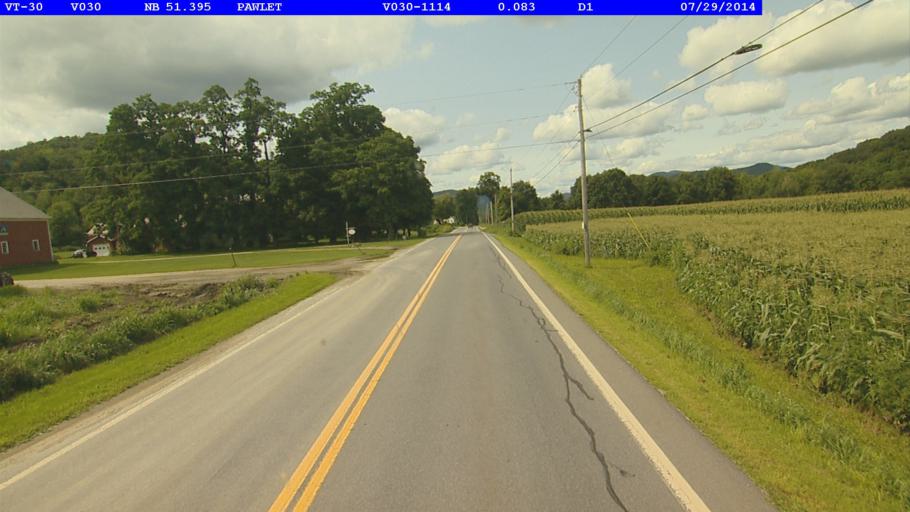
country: US
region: New York
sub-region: Washington County
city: Granville
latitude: 43.3124
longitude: -73.1691
